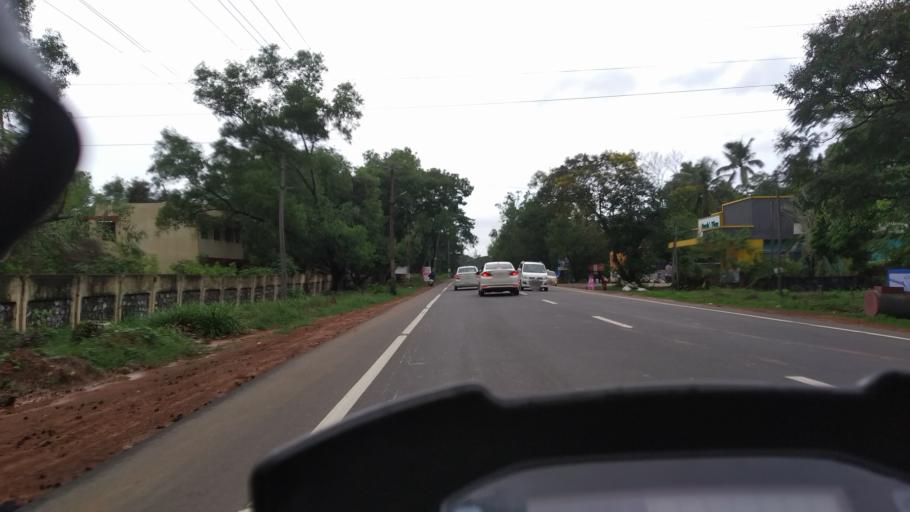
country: IN
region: Kerala
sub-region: Alappuzha
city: Shertallai
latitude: 9.6336
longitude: 76.3339
